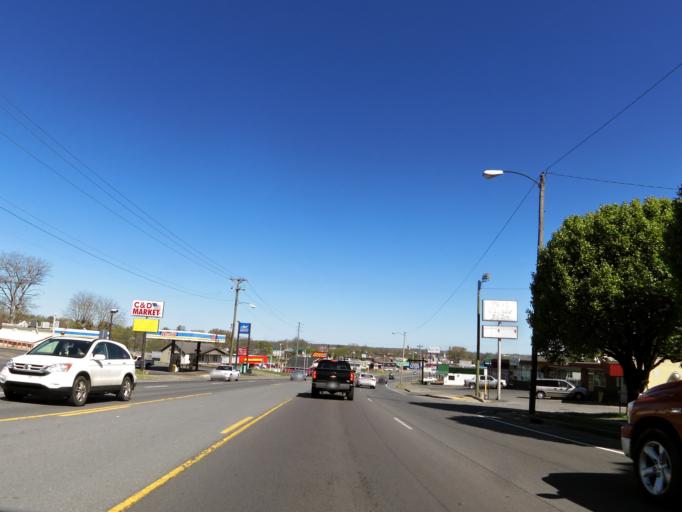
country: US
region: Tennessee
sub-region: Robertson County
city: Springfield
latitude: 36.4970
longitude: -86.8815
